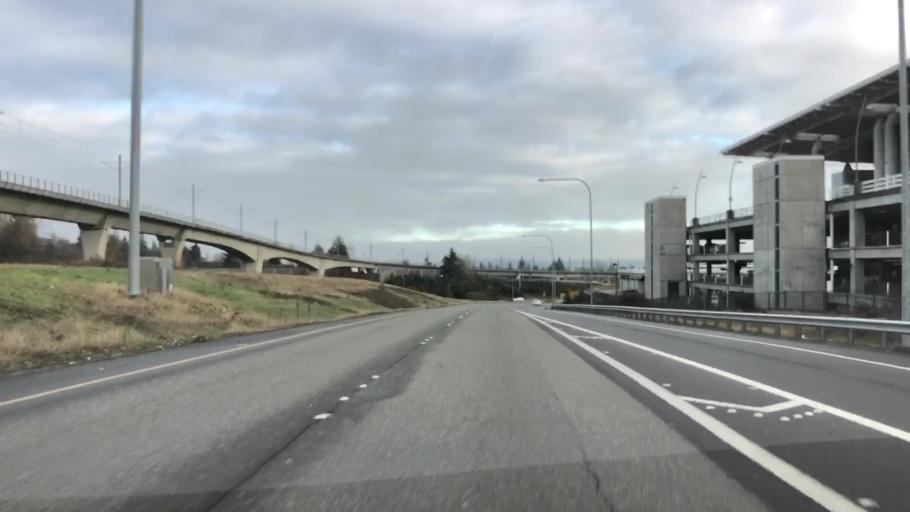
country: US
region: Washington
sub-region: King County
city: SeaTac
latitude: 47.4617
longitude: -122.2945
